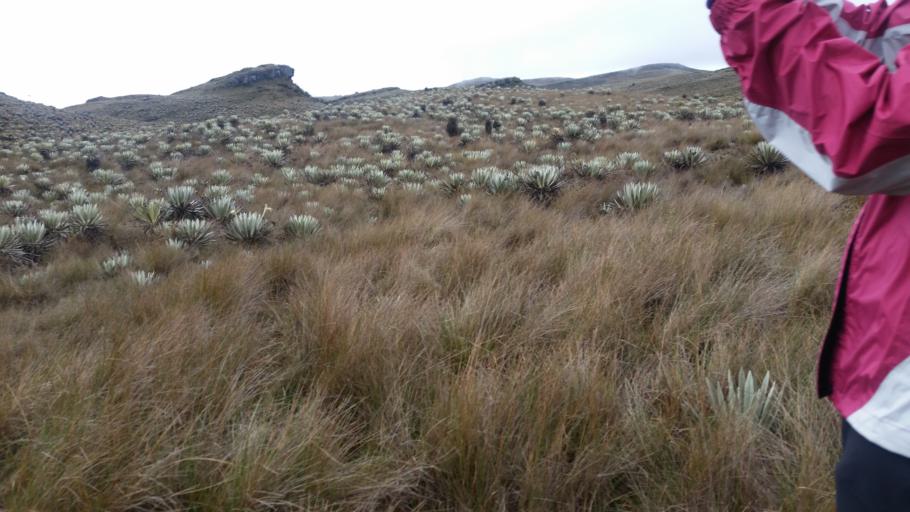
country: CO
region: Cundinamarca
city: Pasca
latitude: 4.3719
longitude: -74.2136
